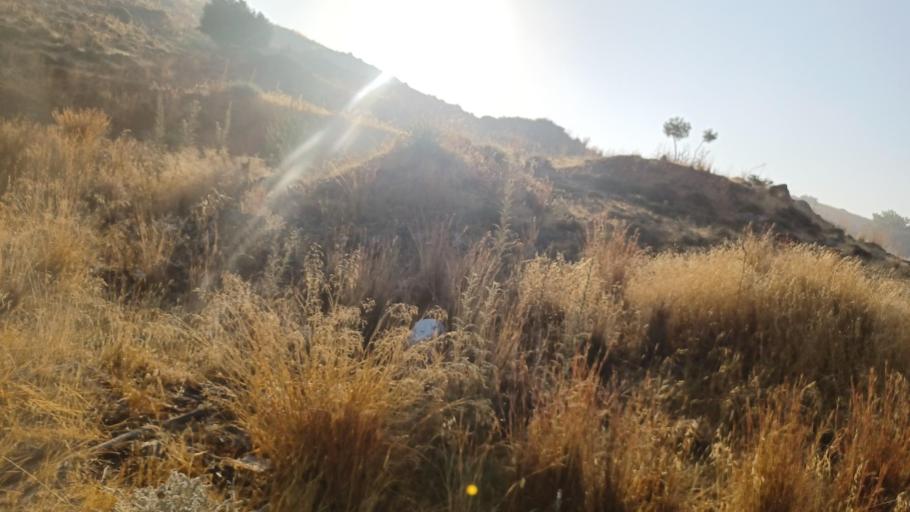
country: CY
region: Larnaka
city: Mosfiloti
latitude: 34.9768
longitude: 33.4297
